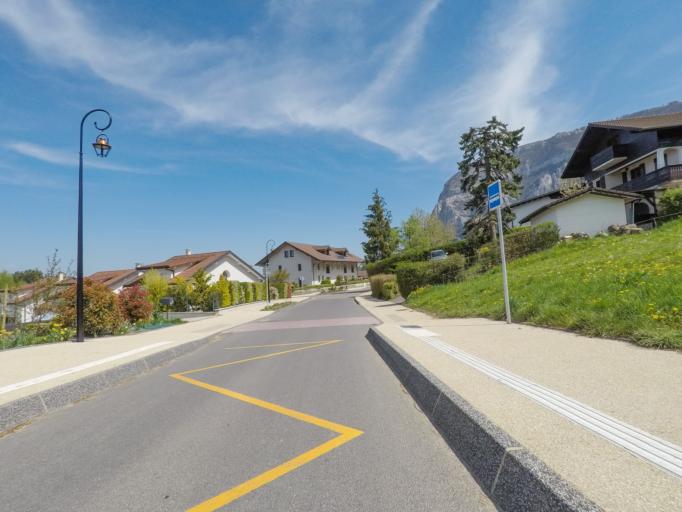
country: FR
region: Rhone-Alpes
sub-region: Departement de la Haute-Savoie
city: Collonges-sous-Saleve
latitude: 46.1267
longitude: 6.1469
